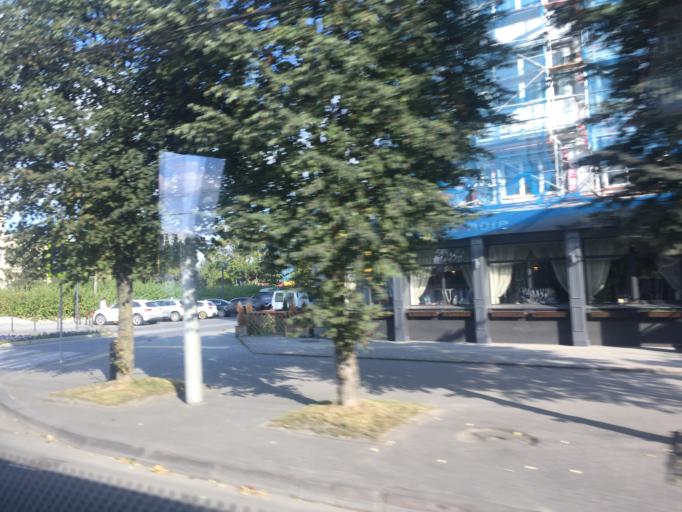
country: RU
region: Kaliningrad
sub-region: Gorod Kaliningrad
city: Kaliningrad
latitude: 54.7040
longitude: 20.5059
